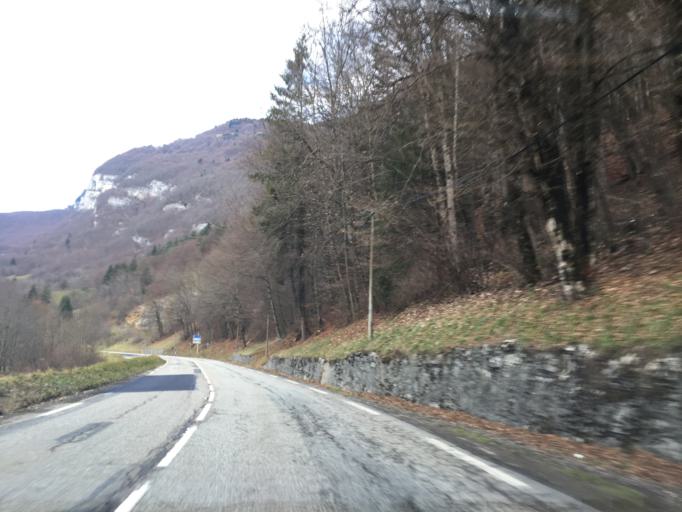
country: FR
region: Rhone-Alpes
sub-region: Departement de la Haute-Savoie
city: Gruffy
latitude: 45.7408
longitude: 6.0985
